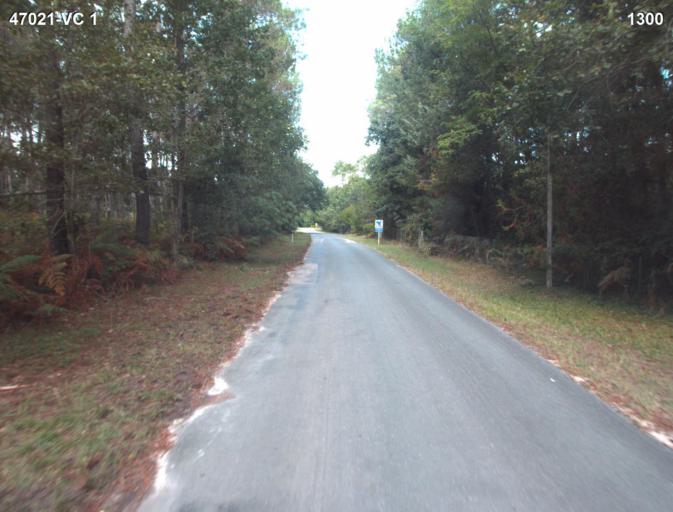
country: FR
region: Aquitaine
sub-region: Departement du Lot-et-Garonne
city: Barbaste
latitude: 44.1552
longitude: 0.2897
